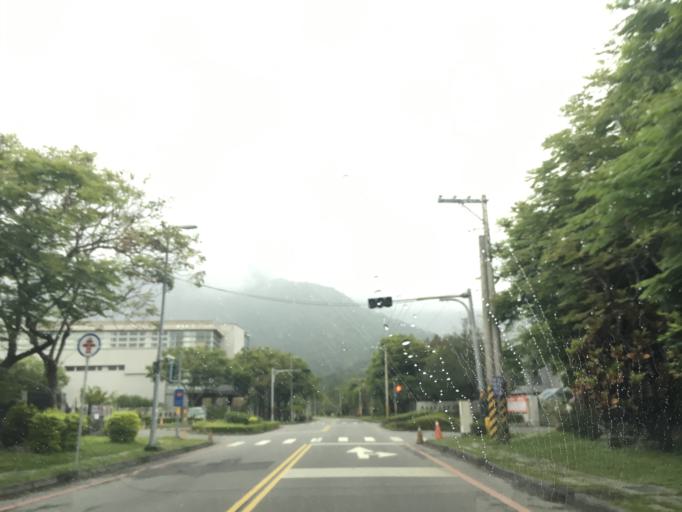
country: TW
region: Taiwan
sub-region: Hualien
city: Hualian
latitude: 23.9992
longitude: 121.5740
